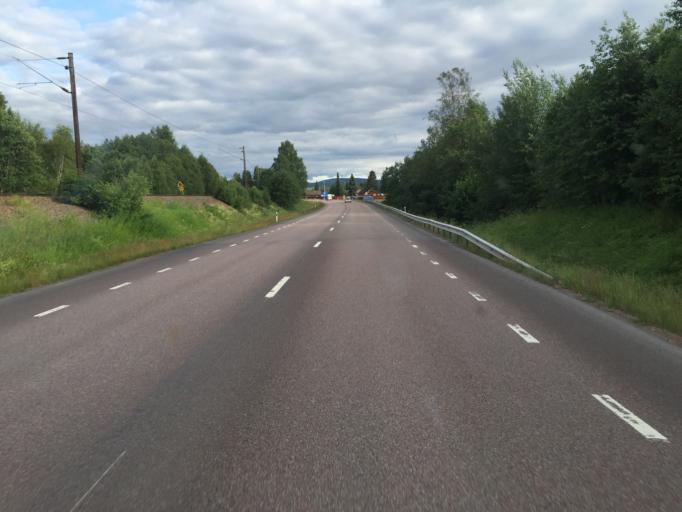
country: SE
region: Dalarna
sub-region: Gagnefs Kommun
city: Djuras
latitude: 60.5682
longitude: 15.1262
